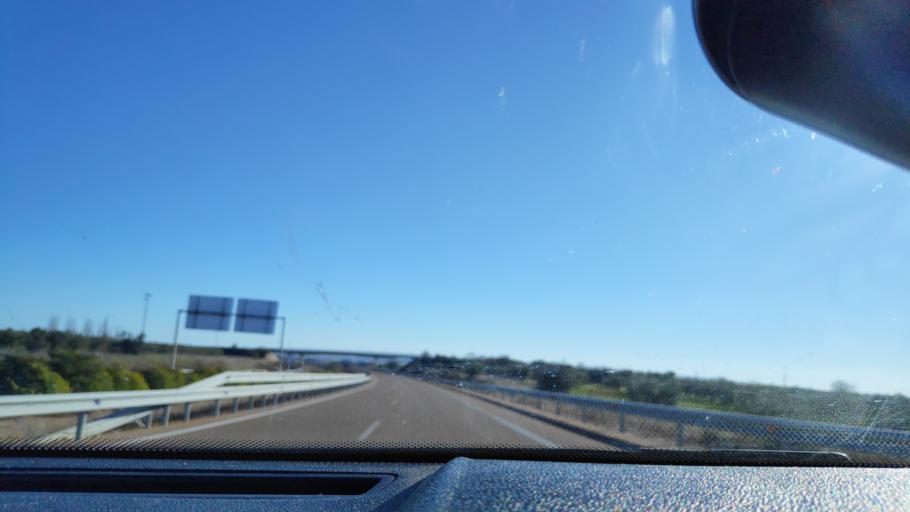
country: ES
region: Extremadura
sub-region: Provincia de Badajoz
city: Puebla de Sancho Perez
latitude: 38.3871
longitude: -6.3403
